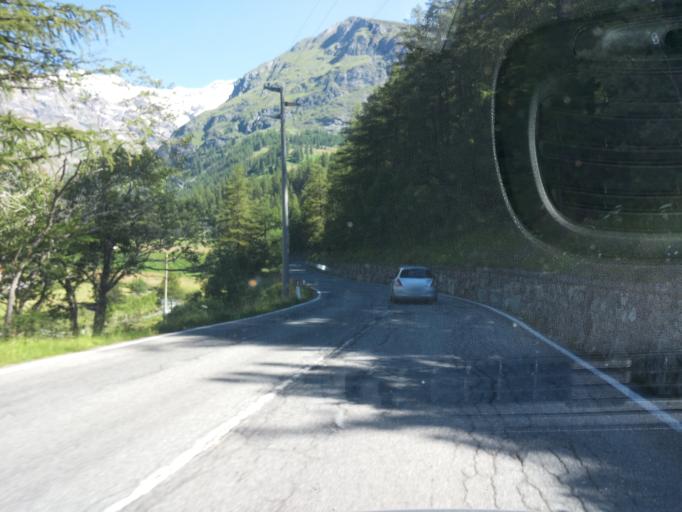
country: IT
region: Aosta Valley
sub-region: Valle d'Aosta
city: Gressoney-La-Trinite
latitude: 45.8513
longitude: 7.8160
